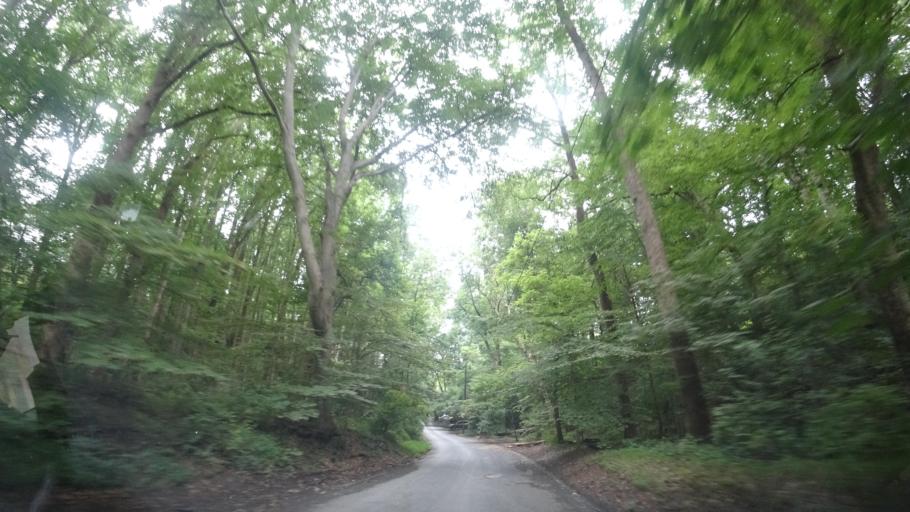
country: US
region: Maryland
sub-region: Montgomery County
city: Potomac
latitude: 39.0330
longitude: -77.2420
